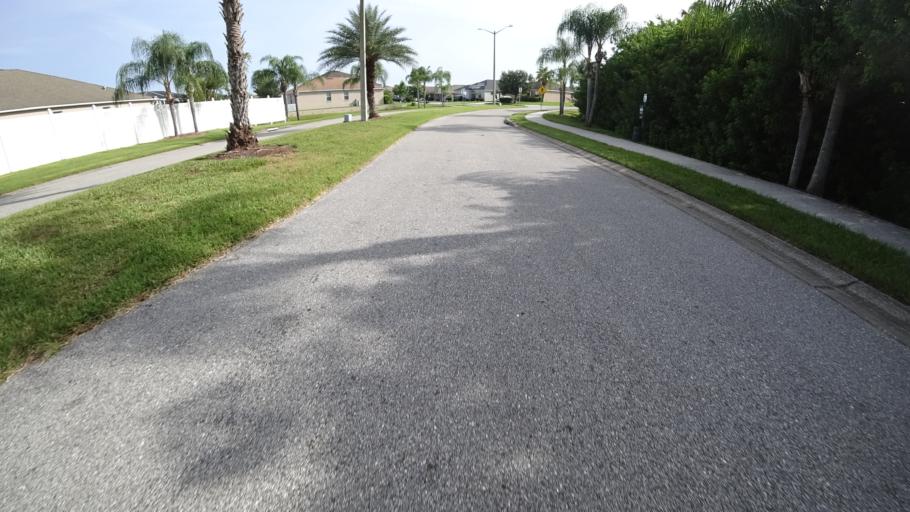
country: US
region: Florida
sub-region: Manatee County
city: Ellenton
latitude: 27.5535
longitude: -82.5015
